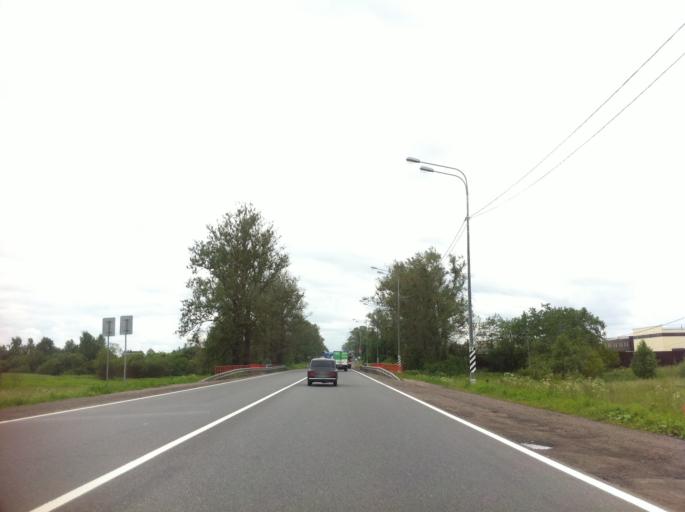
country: RU
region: Leningrad
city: Maloye Verevo
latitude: 59.6192
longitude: 30.1790
